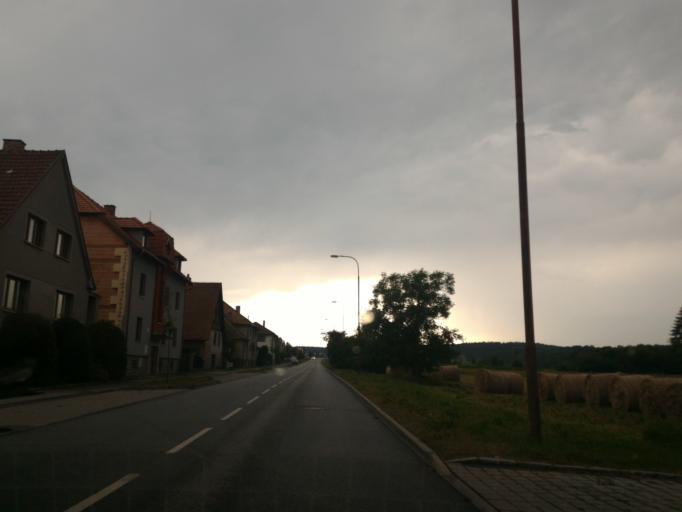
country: CZ
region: Vysocina
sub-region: Okres Jihlava
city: Telc
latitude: 49.1830
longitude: 15.4453
